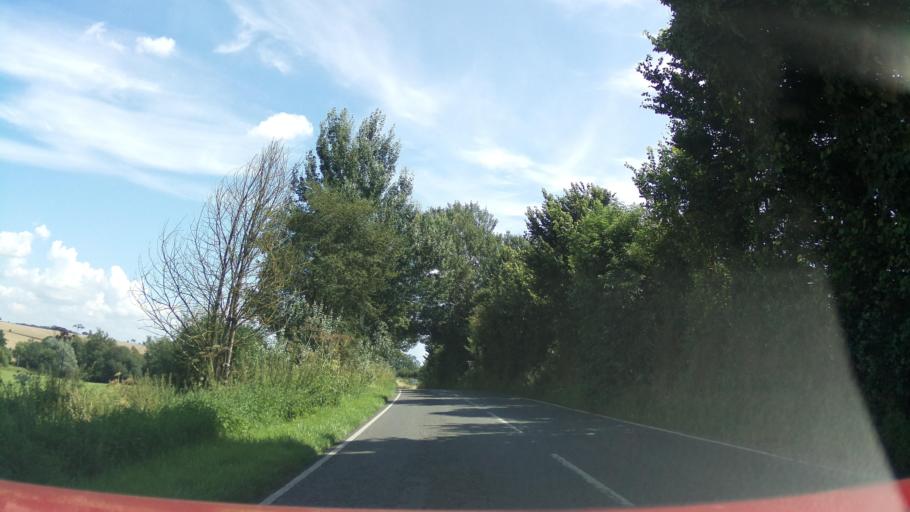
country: GB
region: England
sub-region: West Berkshire
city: Wickham
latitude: 51.4792
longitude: -1.4650
